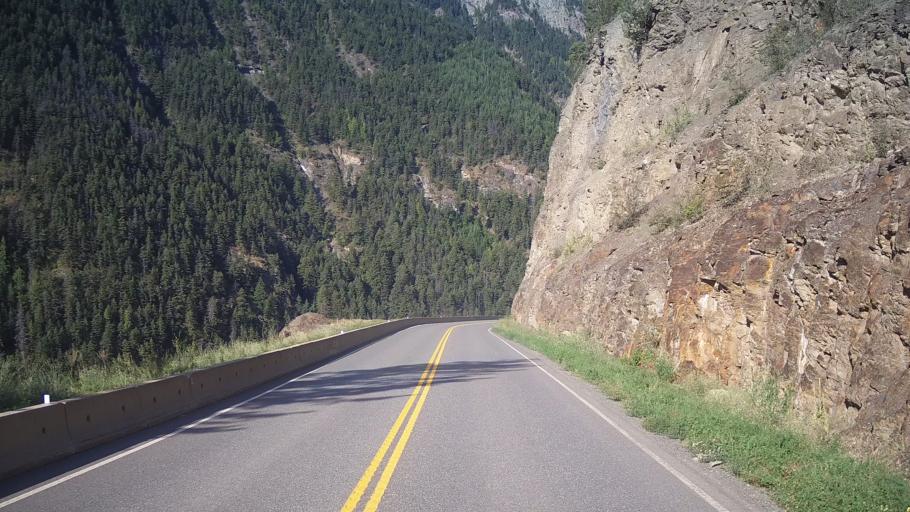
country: CA
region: British Columbia
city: Lillooet
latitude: 50.6422
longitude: -122.0362
